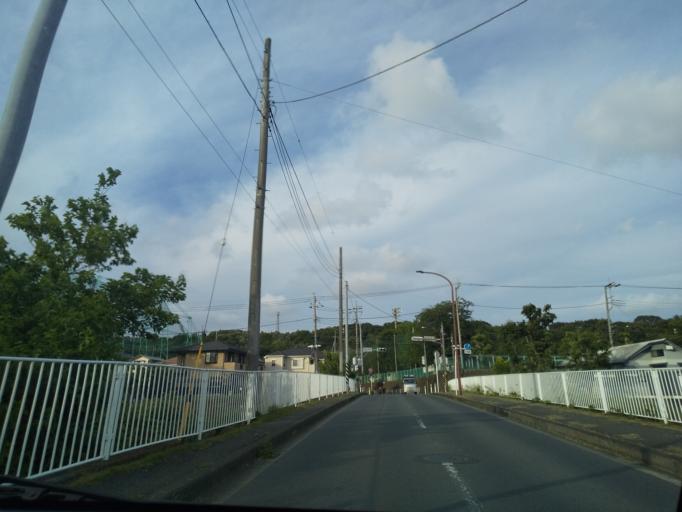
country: JP
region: Kanagawa
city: Zama
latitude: 35.5155
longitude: 139.3838
